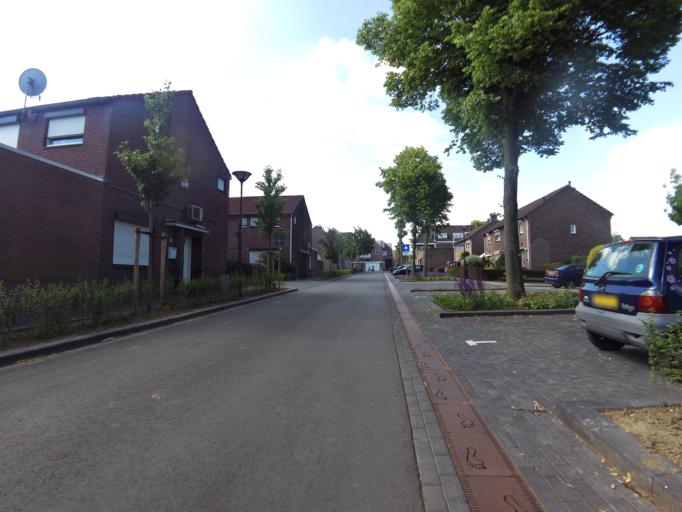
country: NL
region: Limburg
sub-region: Gemeente Heerlen
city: Heerlen
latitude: 50.8991
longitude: 5.9879
